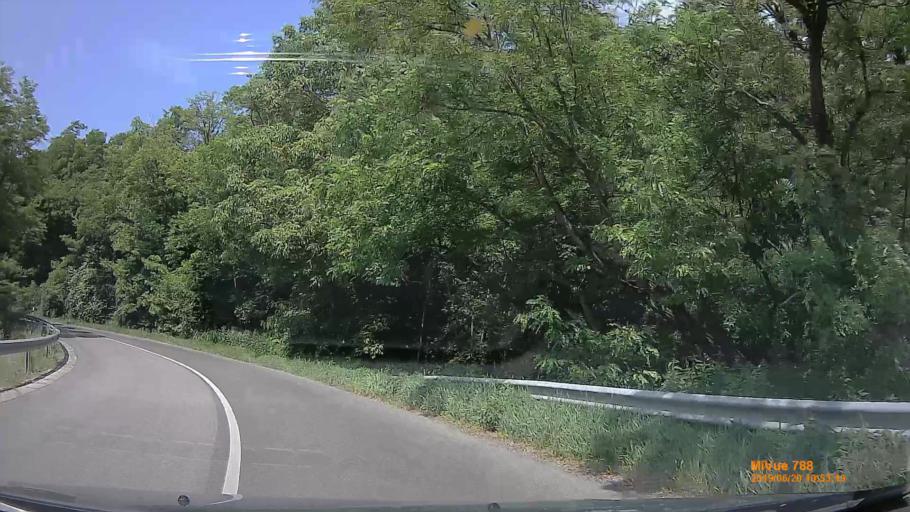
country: HU
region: Baranya
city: Mecseknadasd
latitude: 46.1587
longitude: 18.5736
